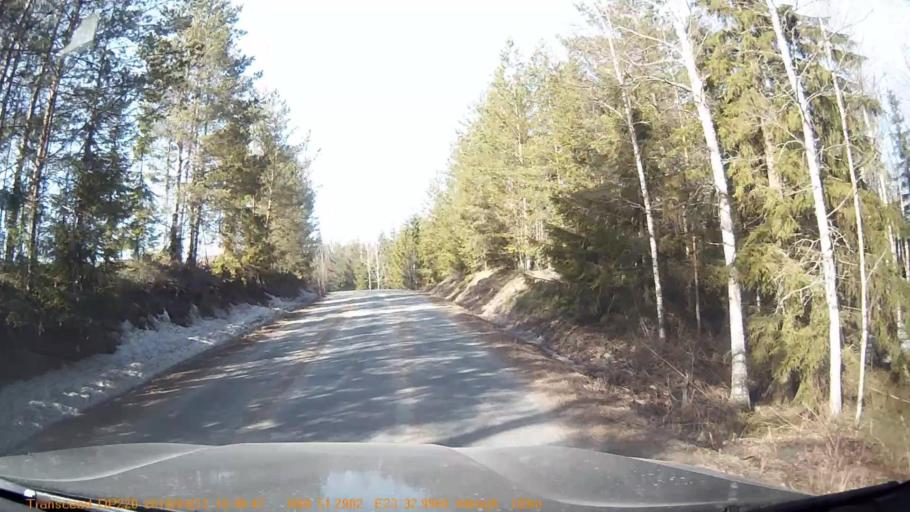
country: FI
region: Haeme
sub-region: Forssa
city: Forssa
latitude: 60.8551
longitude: 23.5500
